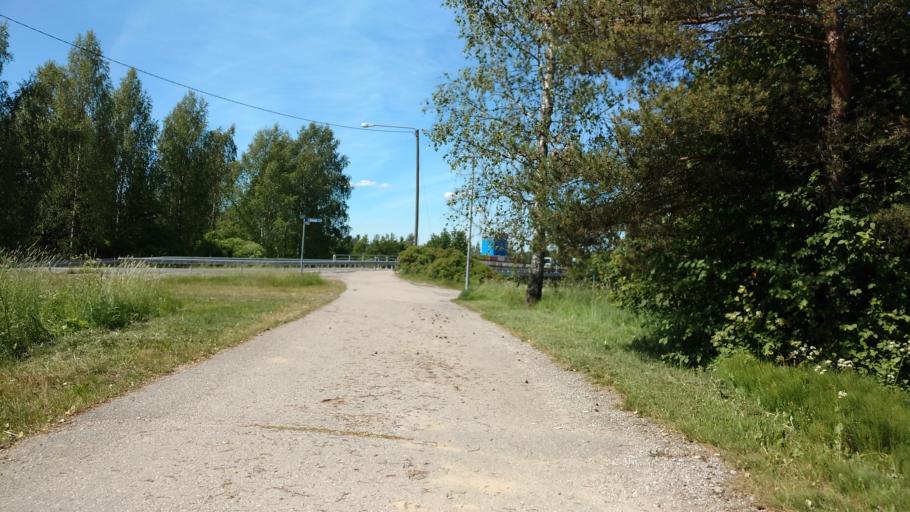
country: FI
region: Varsinais-Suomi
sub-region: Salo
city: Salo
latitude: 60.3926
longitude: 23.1378
